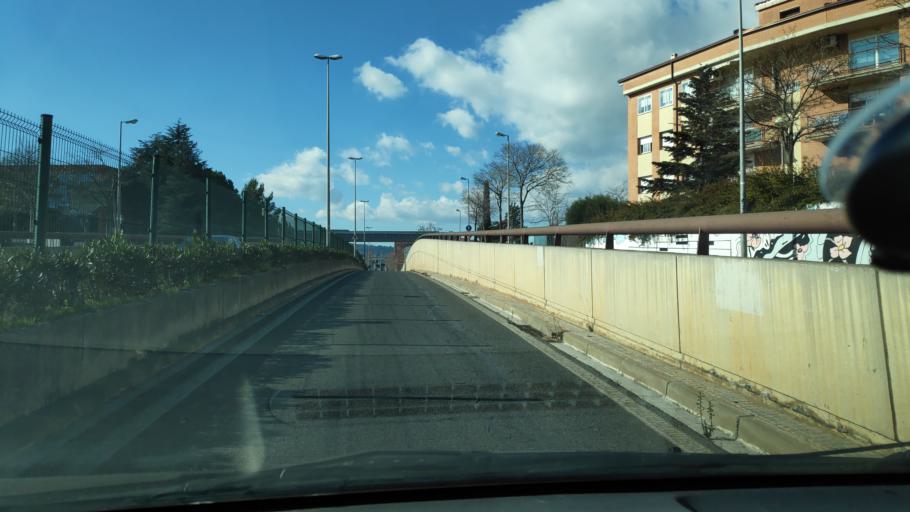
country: ES
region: Catalonia
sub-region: Provincia de Barcelona
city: Terrassa
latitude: 41.5539
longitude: 2.0350
